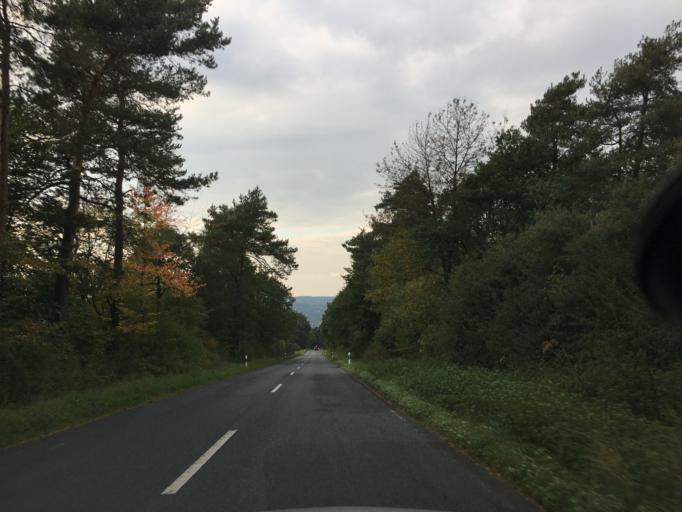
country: DE
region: Hesse
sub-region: Regierungsbezirk Darmstadt
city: Steinau an der Strasse
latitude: 50.3005
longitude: 9.4845
